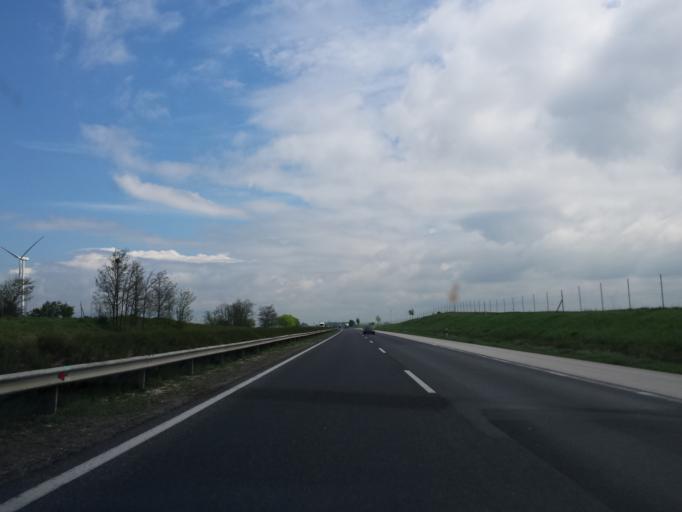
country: HU
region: Komarom-Esztergom
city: Babolna
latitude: 47.6790
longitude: 17.9435
